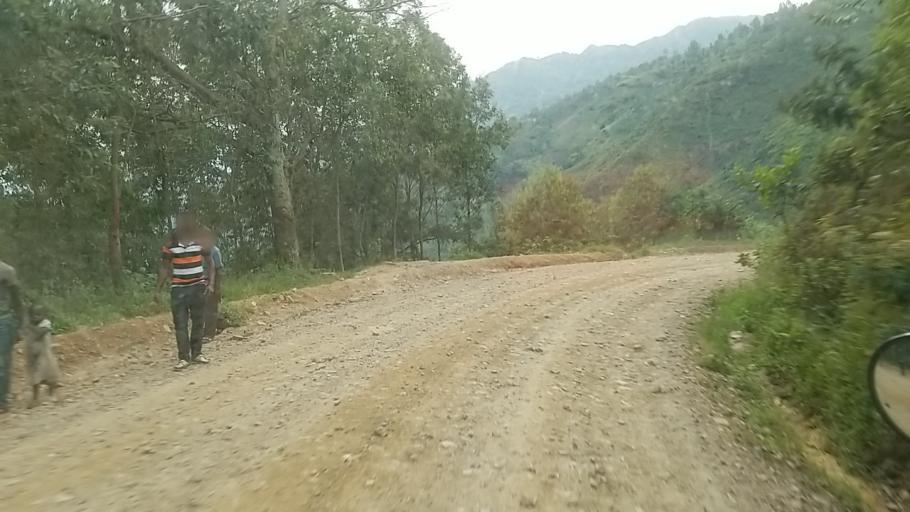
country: CD
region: Nord Kivu
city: Sake
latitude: -1.9650
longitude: 28.9172
